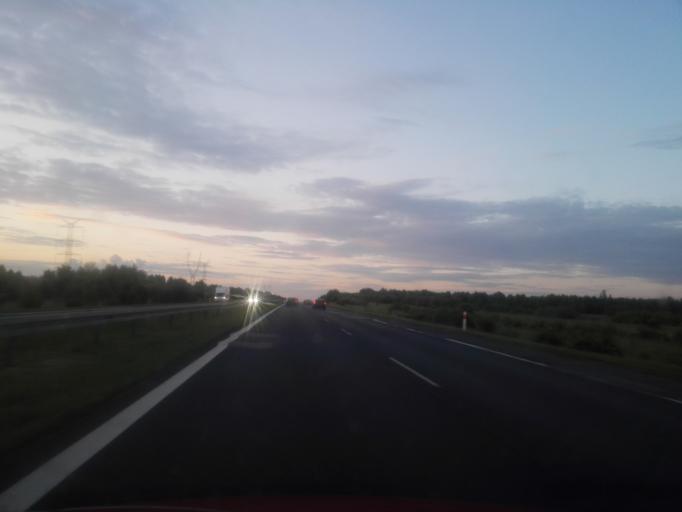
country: PL
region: Lodz Voivodeship
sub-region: Powiat radomszczanski
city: Radomsko
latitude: 51.0858
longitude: 19.3744
